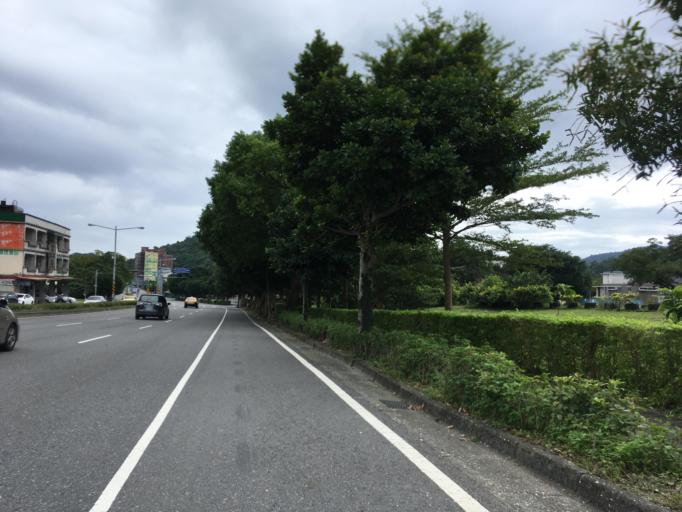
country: TW
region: Taiwan
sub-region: Yilan
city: Yilan
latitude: 24.5952
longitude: 121.8404
